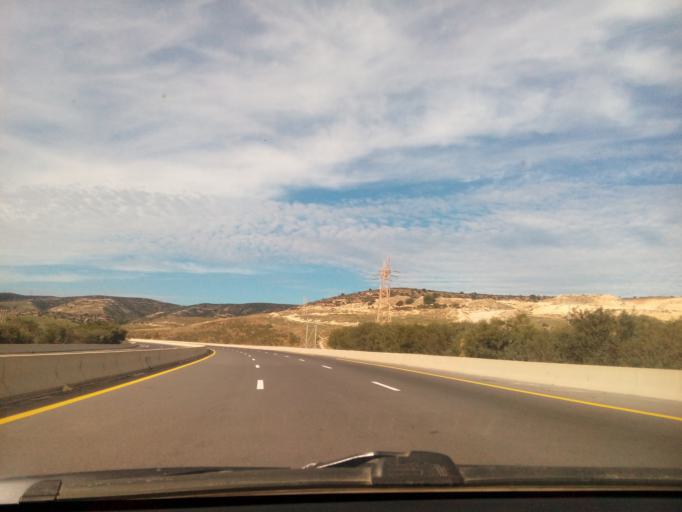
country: DZ
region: Sidi Bel Abbes
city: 'Ain el Berd
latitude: 35.4376
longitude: -0.4392
